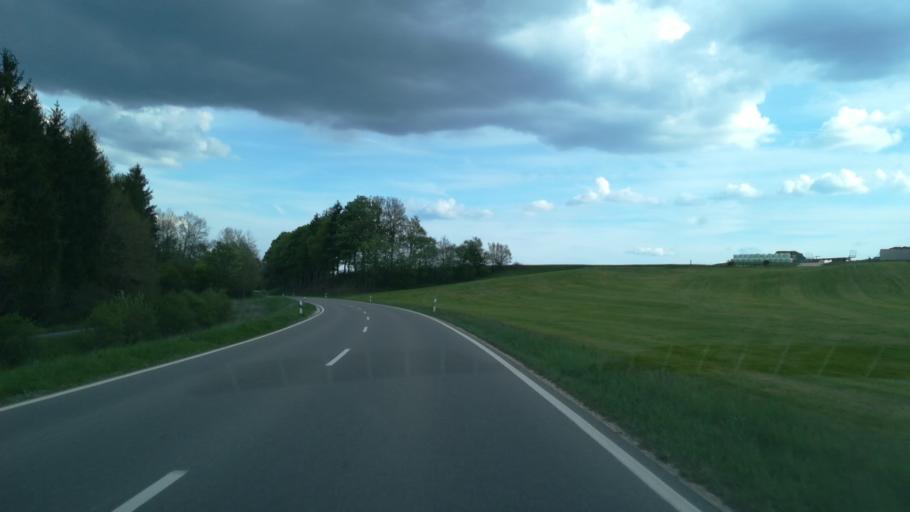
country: DE
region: Baden-Wuerttemberg
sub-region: Tuebingen Region
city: Messkirch
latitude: 48.0136
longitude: 9.1115
